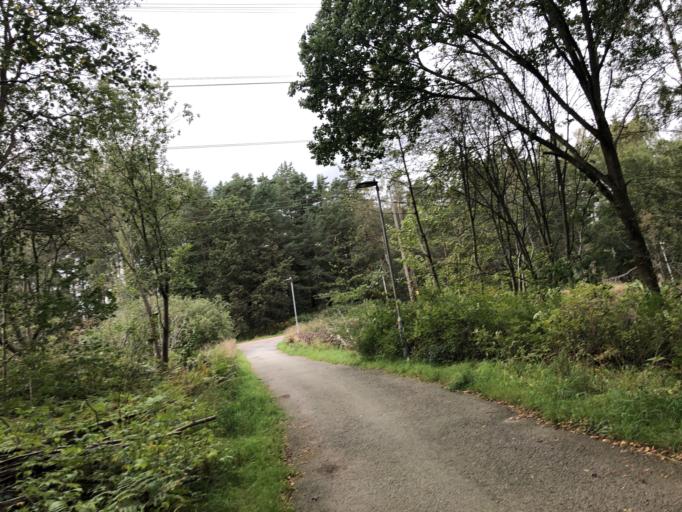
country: SE
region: Vaestra Goetaland
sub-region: Goteborg
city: Majorna
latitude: 57.7402
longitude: 11.8964
